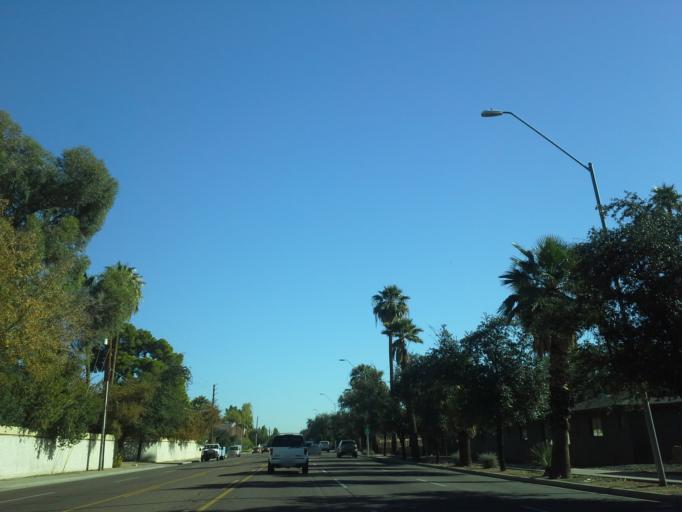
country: US
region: Arizona
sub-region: Maricopa County
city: Phoenix
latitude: 33.4802
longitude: -112.0550
